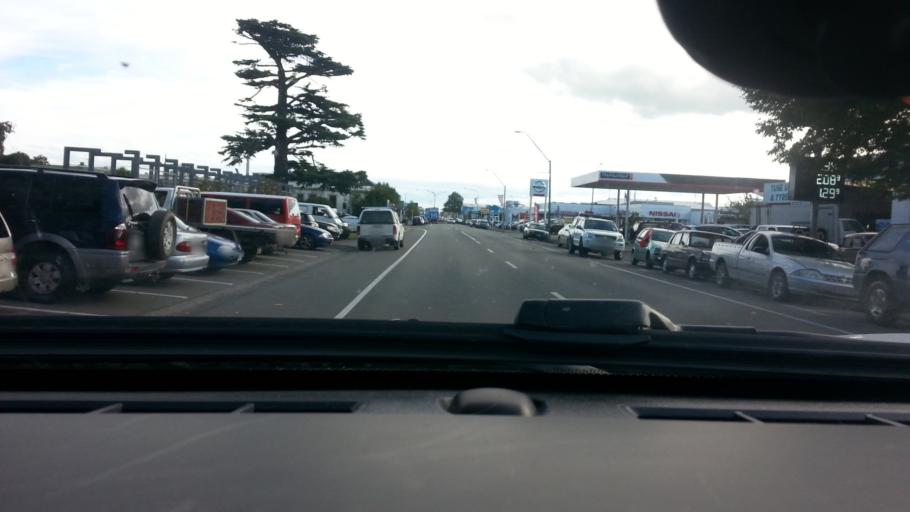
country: NZ
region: Wellington
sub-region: Masterton District
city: Masterton
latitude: -40.9492
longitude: 175.6649
